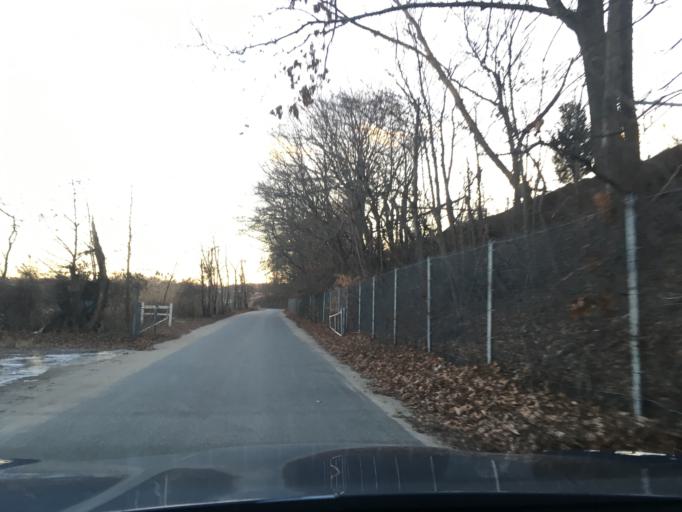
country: US
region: Rhode Island
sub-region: Kent County
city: East Greenwich
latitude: 41.6536
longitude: -71.4521
